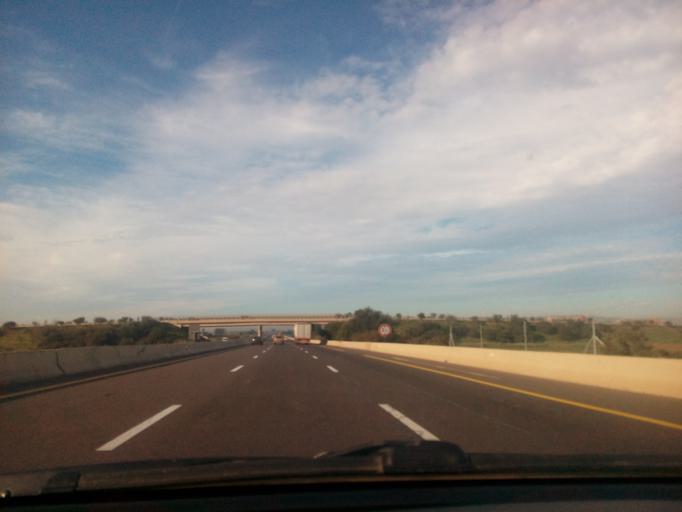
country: DZ
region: Mascara
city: Sig
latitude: 35.5839
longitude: -0.2075
